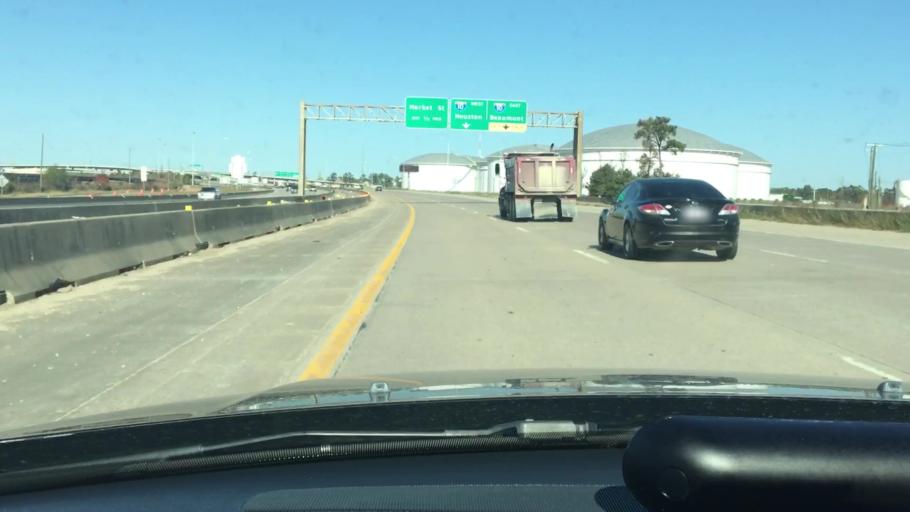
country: US
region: Texas
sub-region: Harris County
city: Cloverleaf
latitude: 29.7597
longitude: -95.1461
